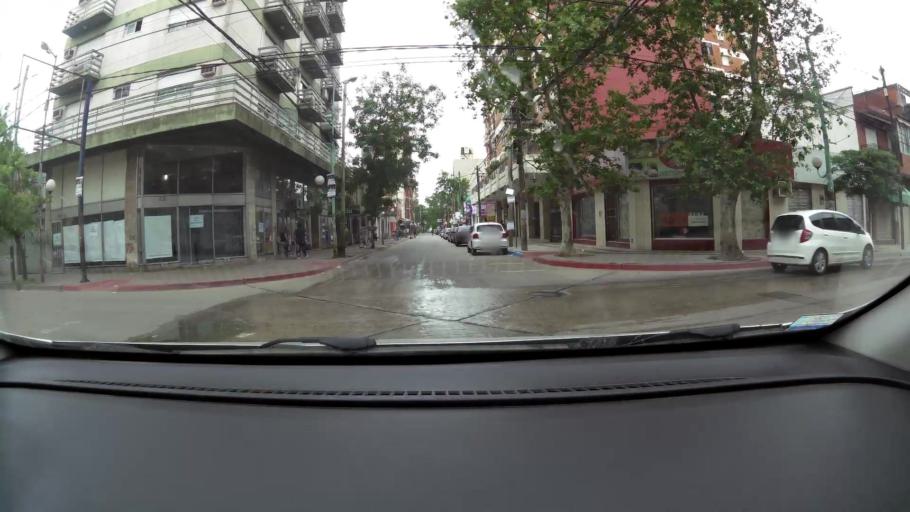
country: AR
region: Buenos Aires
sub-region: Partido de Zarate
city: Zarate
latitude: -34.0993
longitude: -59.0236
